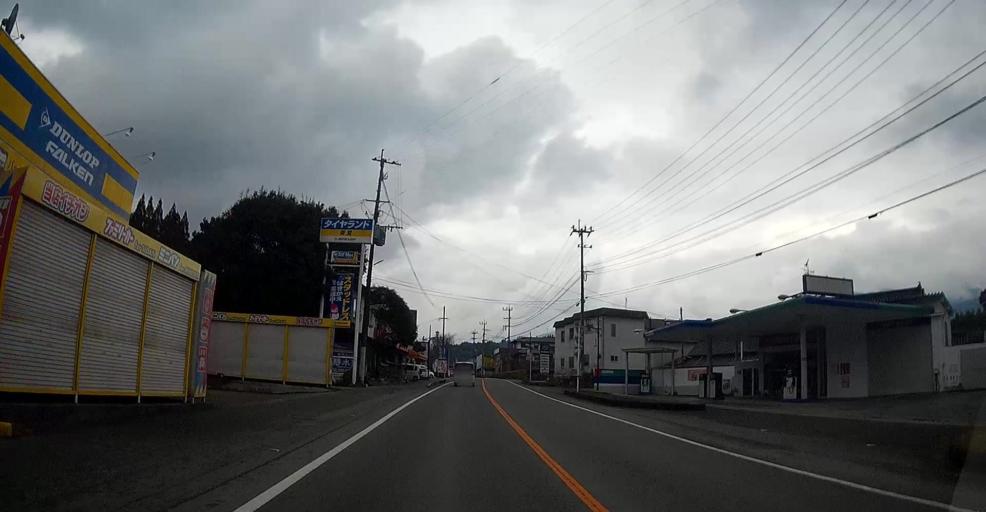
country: JP
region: Kumamoto
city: Matsubase
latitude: 32.6228
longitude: 130.8171
